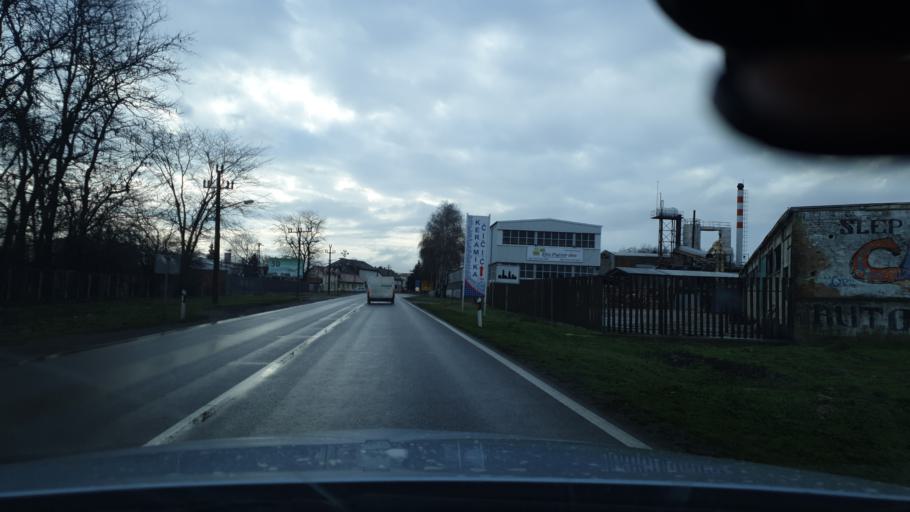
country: RS
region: Autonomna Pokrajina Vojvodina
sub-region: Juznobanatski Okrug
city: Kovin
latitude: 44.7548
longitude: 20.9664
